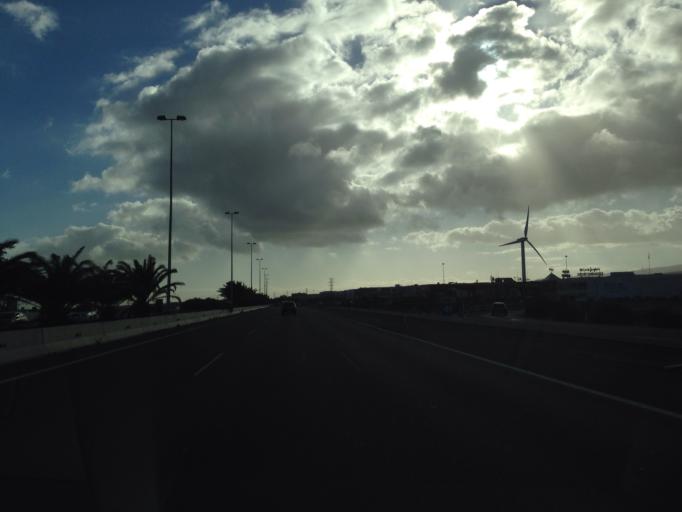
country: ES
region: Canary Islands
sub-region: Provincia de Las Palmas
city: Cruce de Arinaga
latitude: 27.8656
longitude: -15.4228
